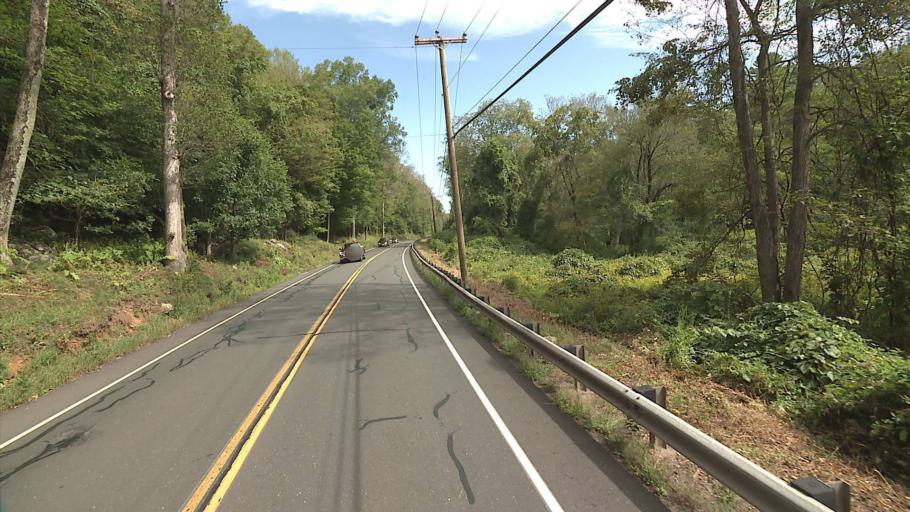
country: US
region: Connecticut
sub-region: Tolland County
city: Stafford Springs
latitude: 41.9385
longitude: -72.3078
